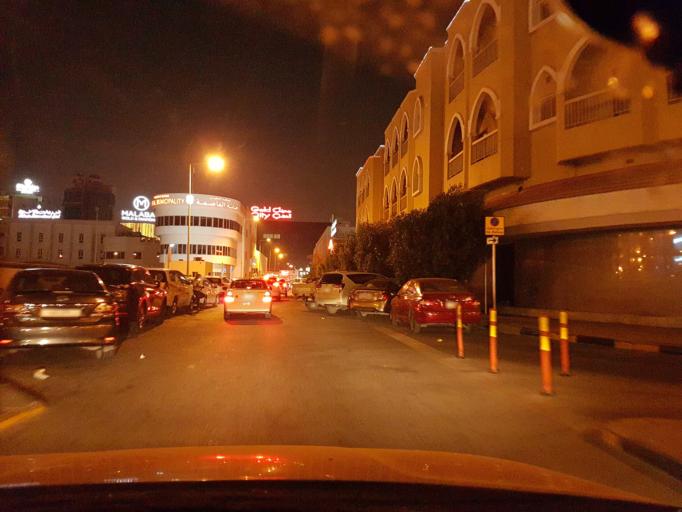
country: BH
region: Manama
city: Manama
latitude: 26.2340
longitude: 50.5713
